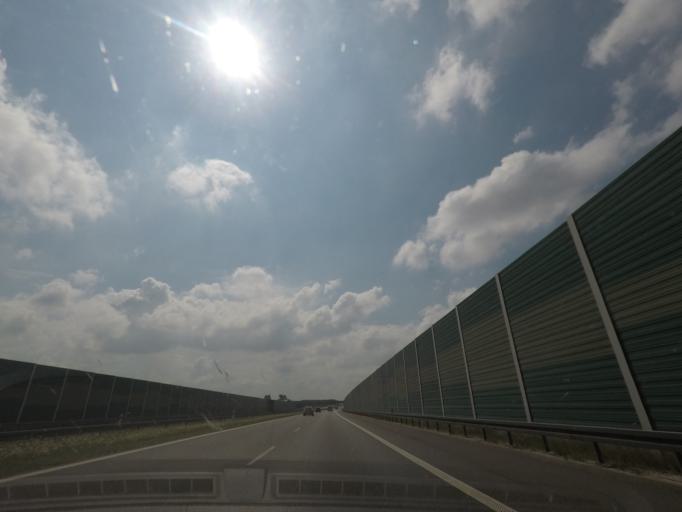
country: PL
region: Lodz Voivodeship
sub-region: Powiat kutnowski
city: Krzyzanow
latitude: 52.2038
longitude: 19.4841
